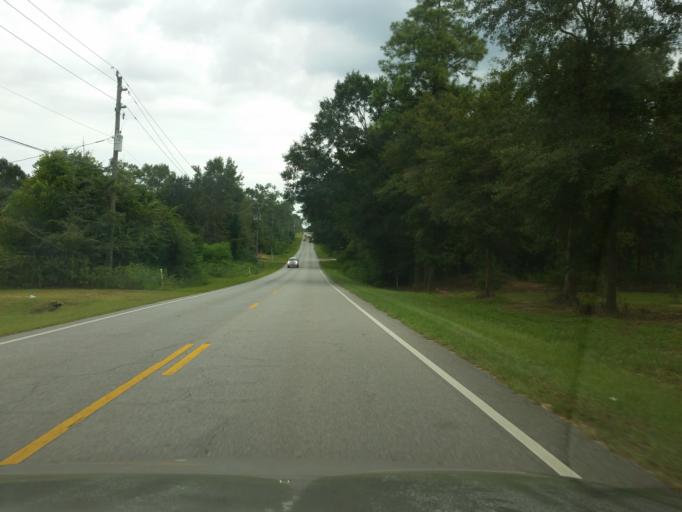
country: US
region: Florida
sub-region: Escambia County
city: Molino
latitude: 30.7095
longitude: -87.3354
